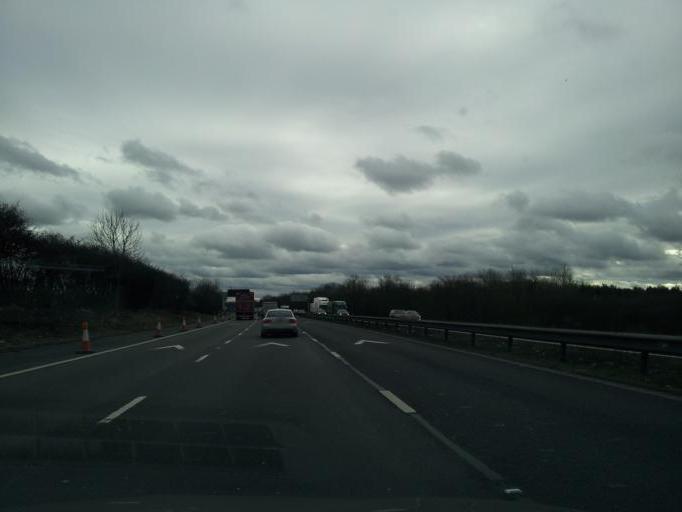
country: GB
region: England
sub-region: Staffordshire
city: Stone
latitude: 52.9078
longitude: -2.1921
